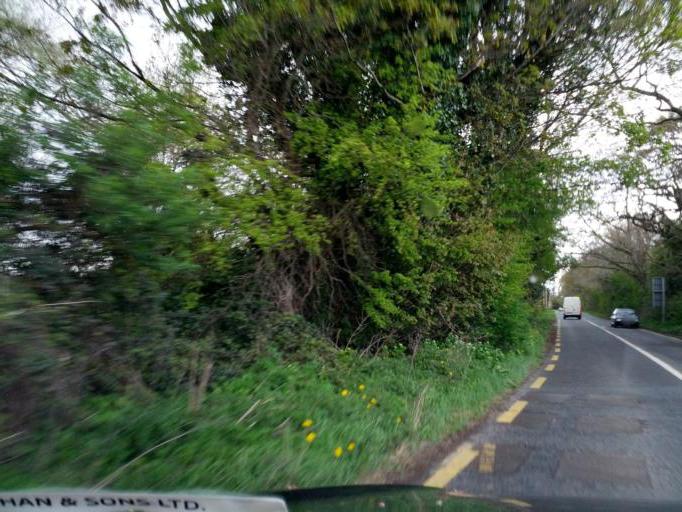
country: IE
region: Leinster
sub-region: An Mhi
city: Dunboyne
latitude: 53.3905
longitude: -6.4487
